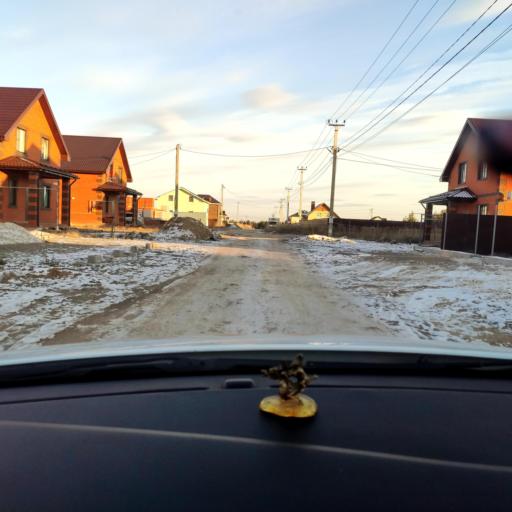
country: RU
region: Tatarstan
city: Stolbishchi
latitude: 55.6035
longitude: 49.1425
